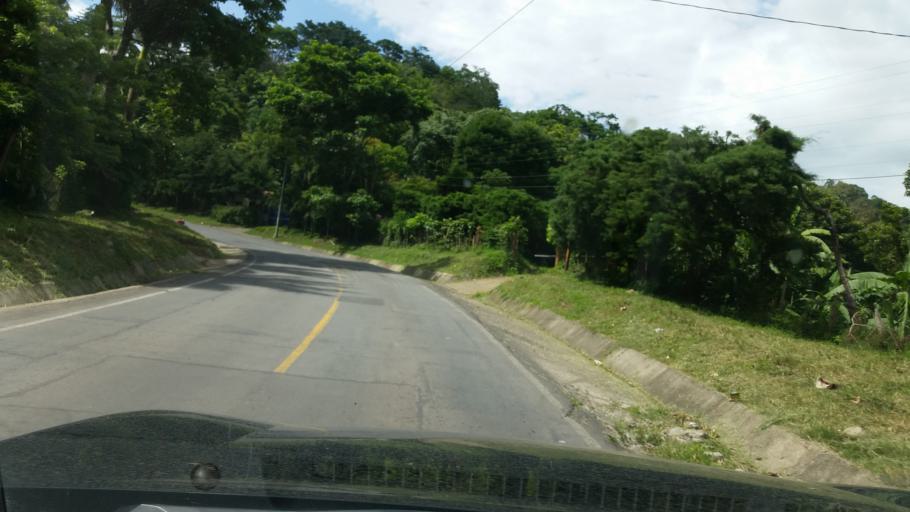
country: NI
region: Matagalpa
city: San Ramon
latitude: 12.9537
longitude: -85.8714
